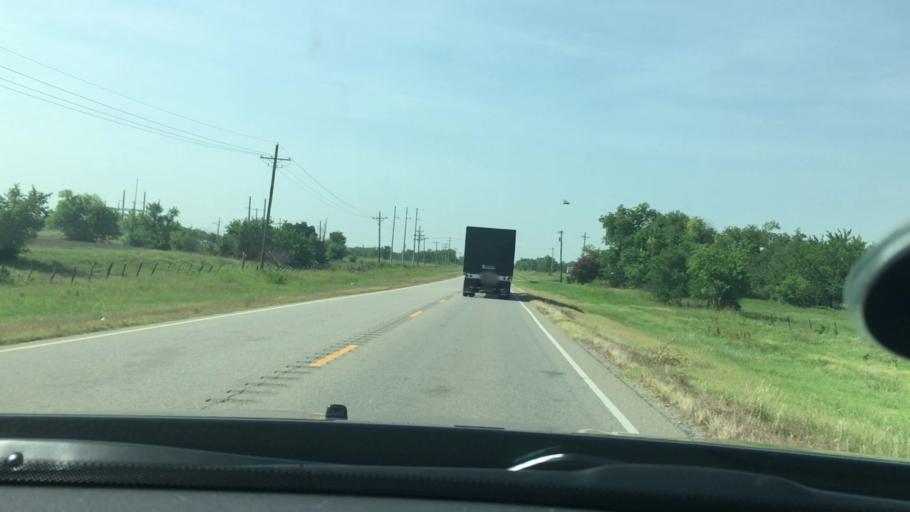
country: US
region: Oklahoma
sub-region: Coal County
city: Coalgate
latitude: 34.4877
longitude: -96.2187
